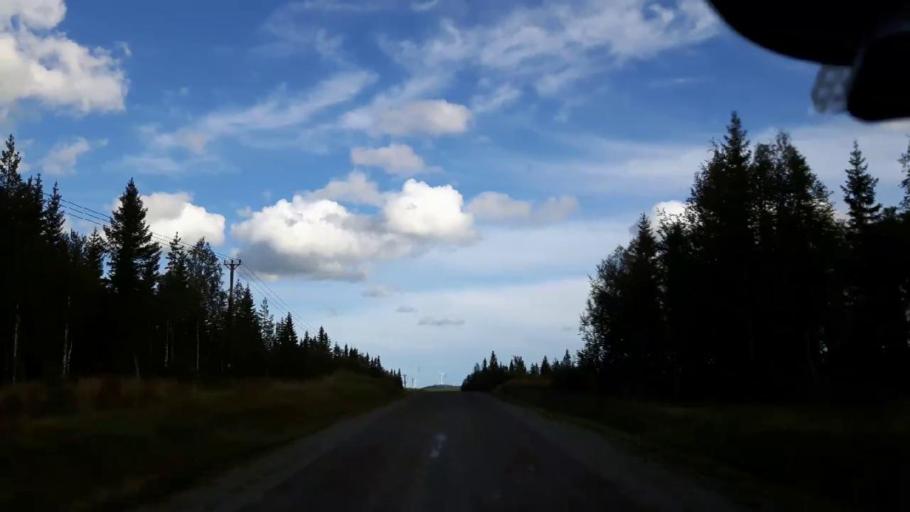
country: SE
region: Jaemtland
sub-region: Ragunda Kommun
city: Hammarstrand
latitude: 63.4392
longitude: 15.9943
